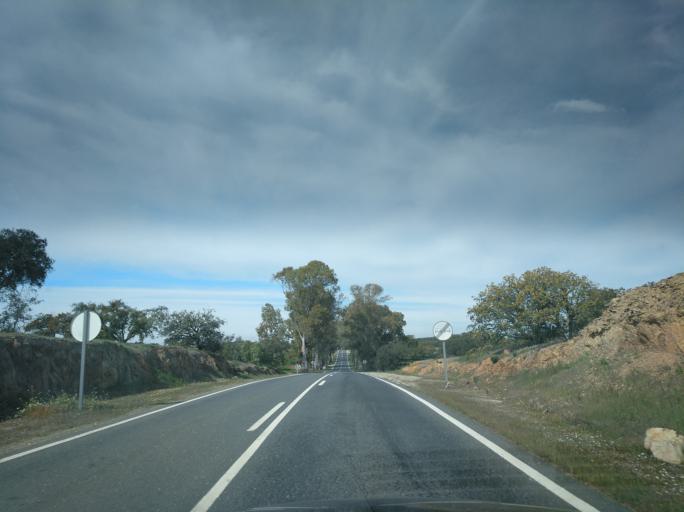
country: PT
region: Beja
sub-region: Mertola
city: Mertola
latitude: 37.7237
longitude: -7.7632
